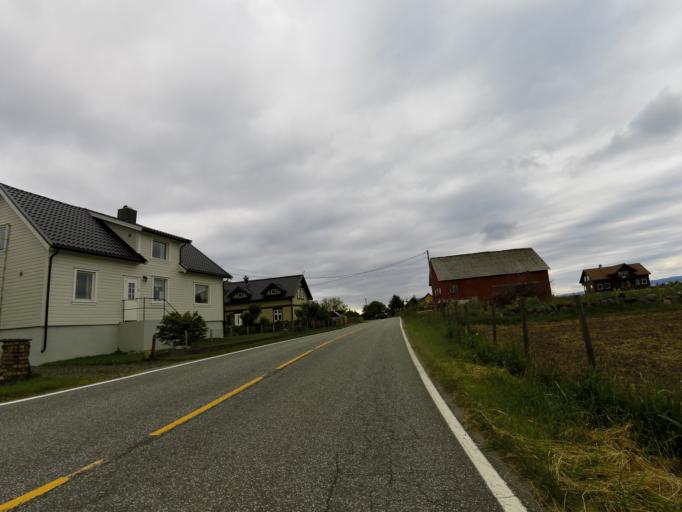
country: NO
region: Vest-Agder
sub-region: Farsund
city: Vestbygd
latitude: 58.1213
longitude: 6.6015
